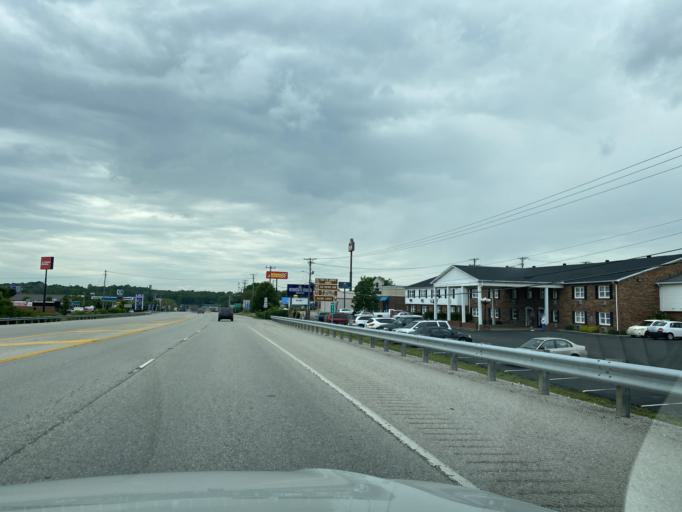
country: US
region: Kentucky
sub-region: Scott County
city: Georgetown
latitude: 38.2157
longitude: -84.5367
